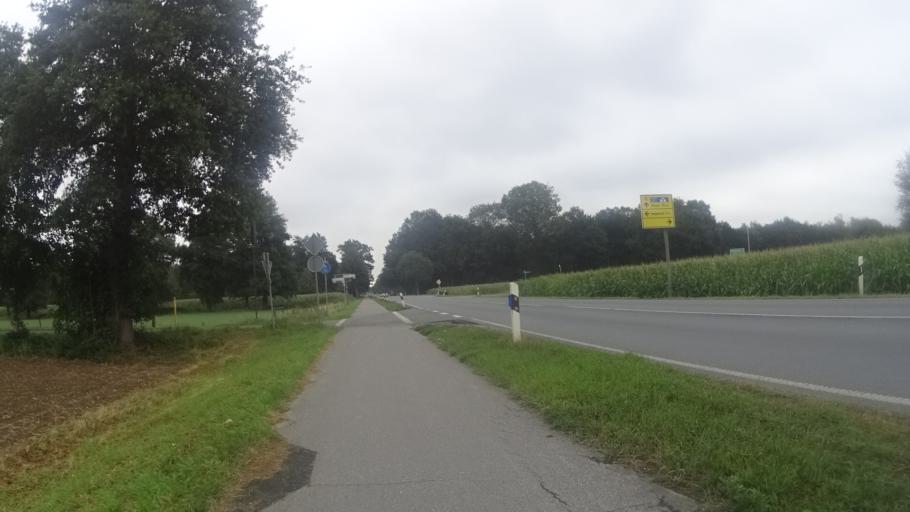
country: DE
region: North Rhine-Westphalia
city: Geldern
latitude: 51.5252
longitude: 6.3708
